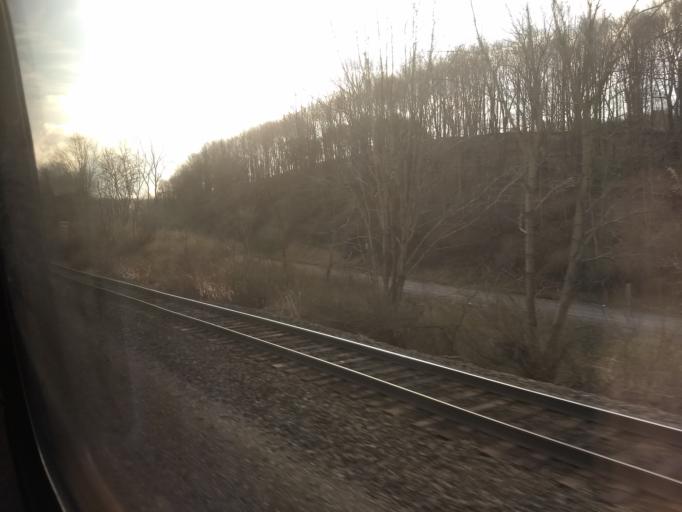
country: US
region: Pennsylvania
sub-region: Cambria County
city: Salix
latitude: 40.3762
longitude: -78.7550
